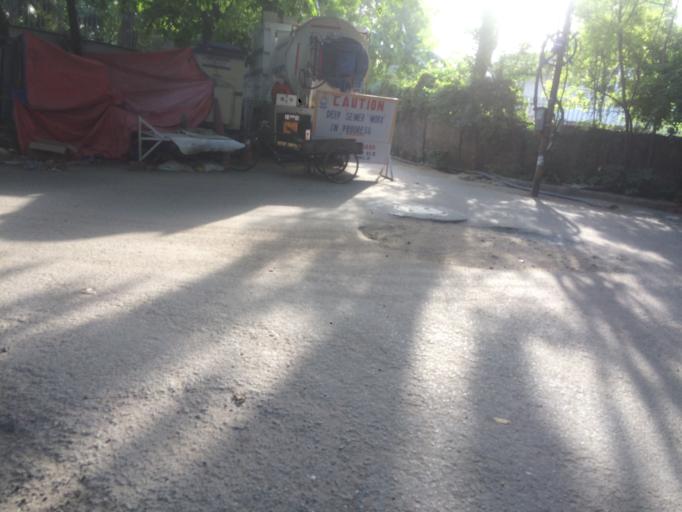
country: IN
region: Uttar Pradesh
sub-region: Gautam Buddha Nagar
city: Noida
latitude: 28.5672
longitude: 77.2642
